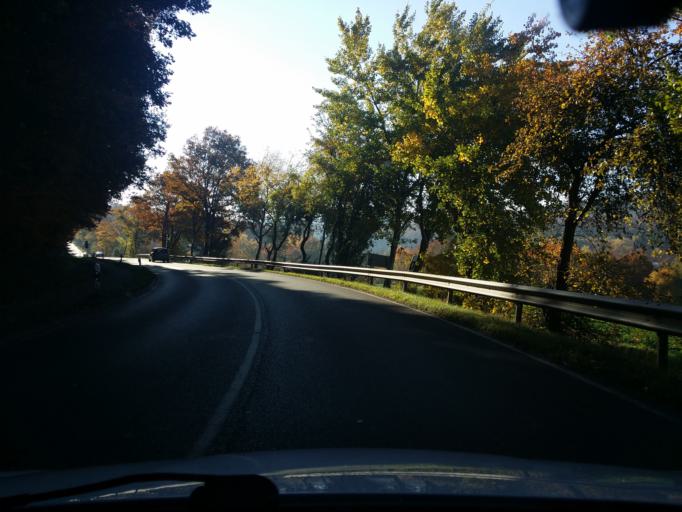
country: DE
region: Hesse
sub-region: Regierungsbezirk Darmstadt
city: Niedernhausen
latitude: 50.1804
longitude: 8.2952
